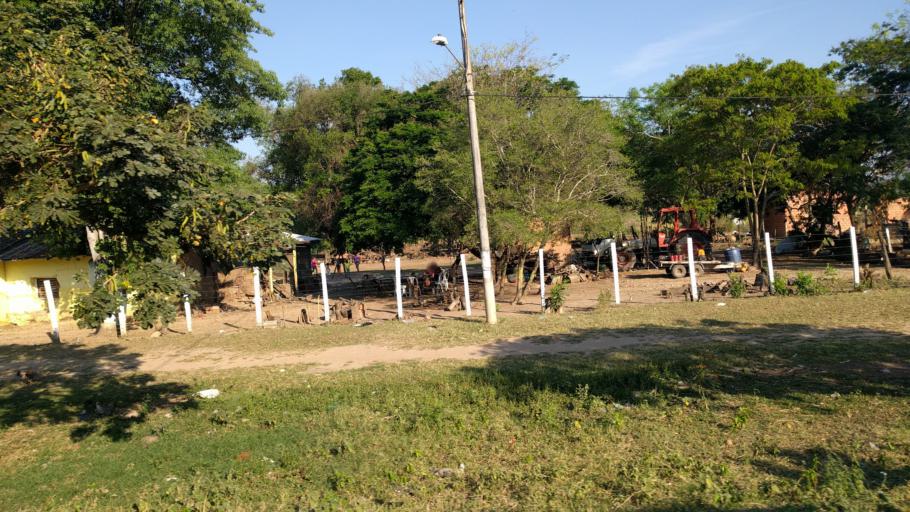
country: BO
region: Santa Cruz
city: Jorochito
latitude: -18.1384
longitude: -63.4767
